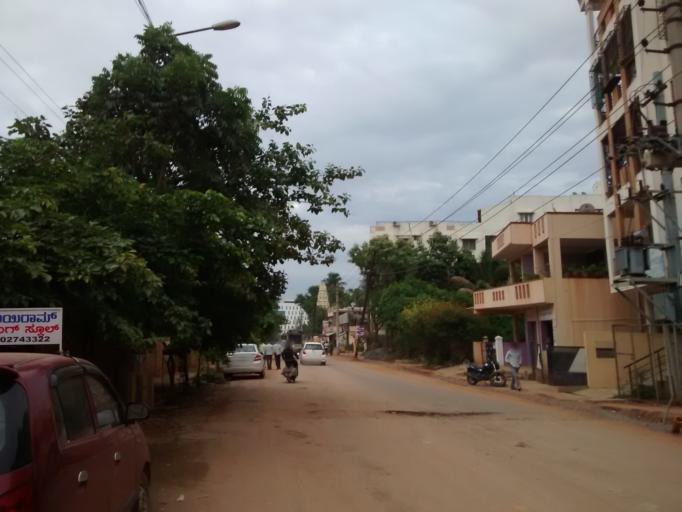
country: IN
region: Karnataka
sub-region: Bangalore Urban
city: Bangalore
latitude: 12.9488
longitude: 77.6852
